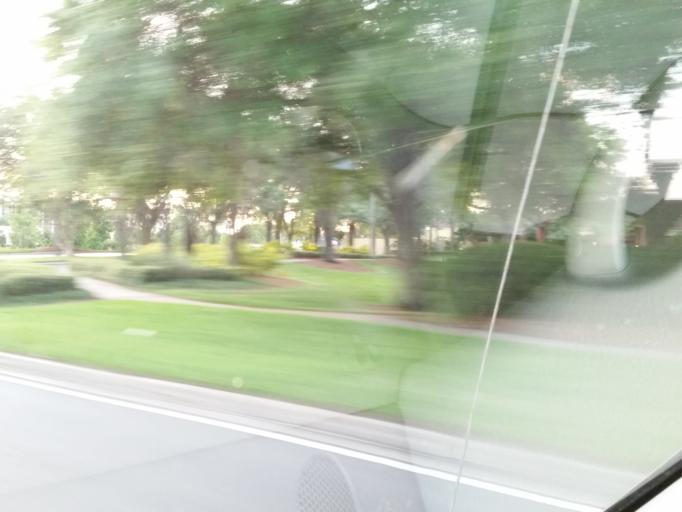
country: US
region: Florida
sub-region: Orange County
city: Doctor Phillips
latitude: 28.3857
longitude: -81.5022
